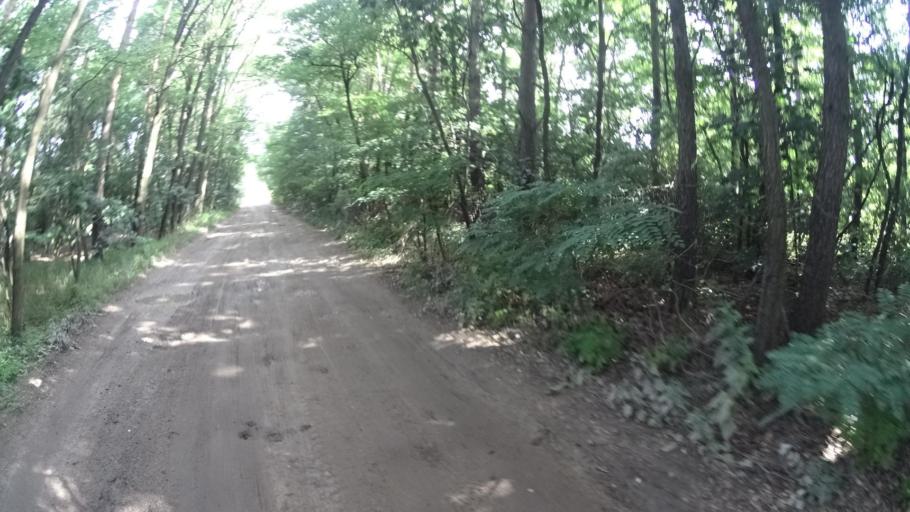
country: PL
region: Masovian Voivodeship
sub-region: Powiat piaseczynski
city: Tarczyn
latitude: 51.9671
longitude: 20.8542
